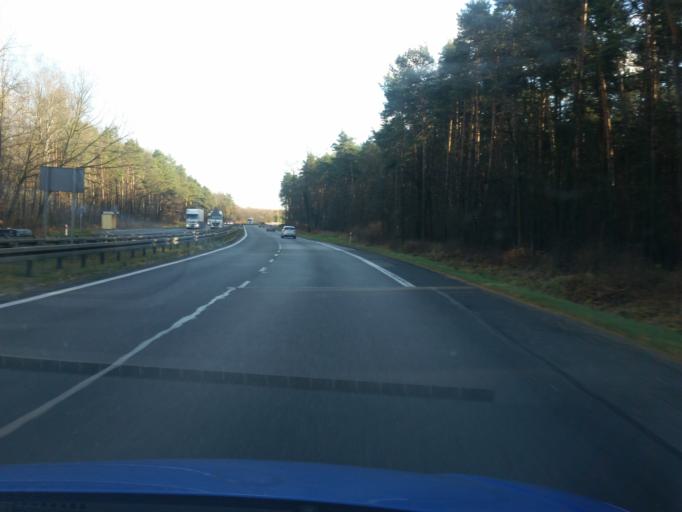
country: PL
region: Silesian Voivodeship
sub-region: Powiat myszkowski
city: Kozieglowy
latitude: 50.5395
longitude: 19.1825
